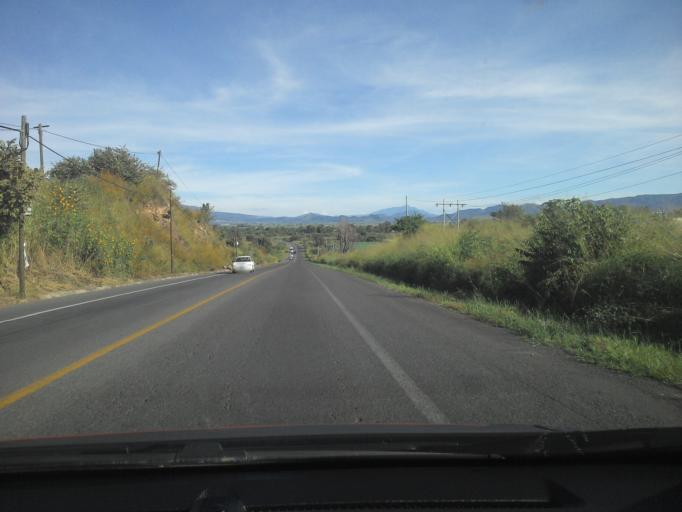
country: MX
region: Jalisco
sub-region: Teuchitlan
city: La Estanzuela
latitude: 20.6775
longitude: -103.8368
